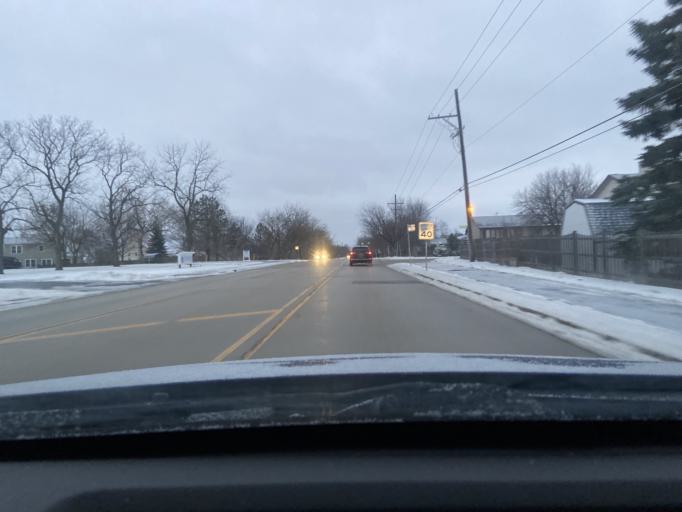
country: US
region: Illinois
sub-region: Lake County
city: Grayslake
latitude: 42.3509
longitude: -88.0241
